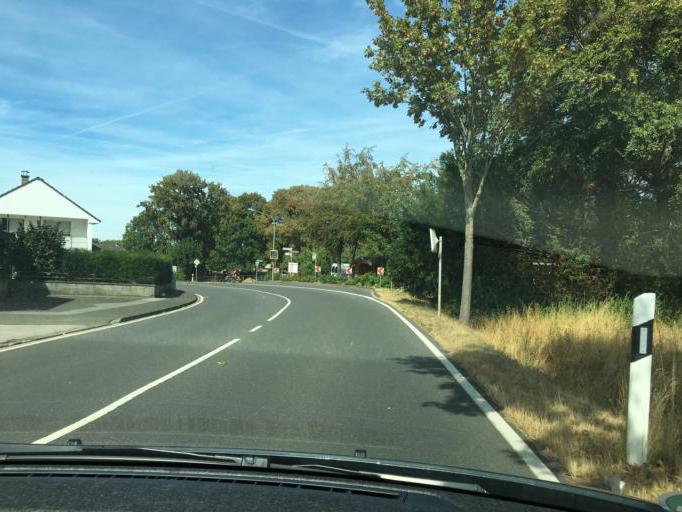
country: DE
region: North Rhine-Westphalia
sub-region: Regierungsbezirk Koln
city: Hurtgenwald
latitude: 50.7348
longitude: 6.3966
